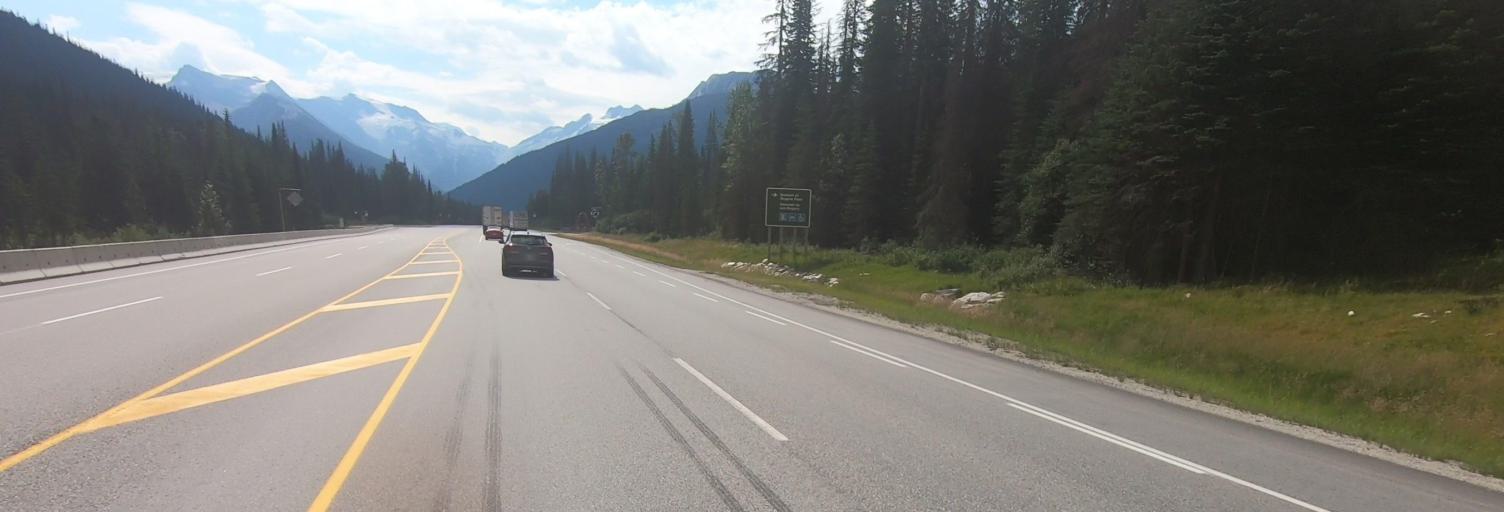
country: CA
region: British Columbia
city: Golden
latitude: 51.2921
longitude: -117.5162
